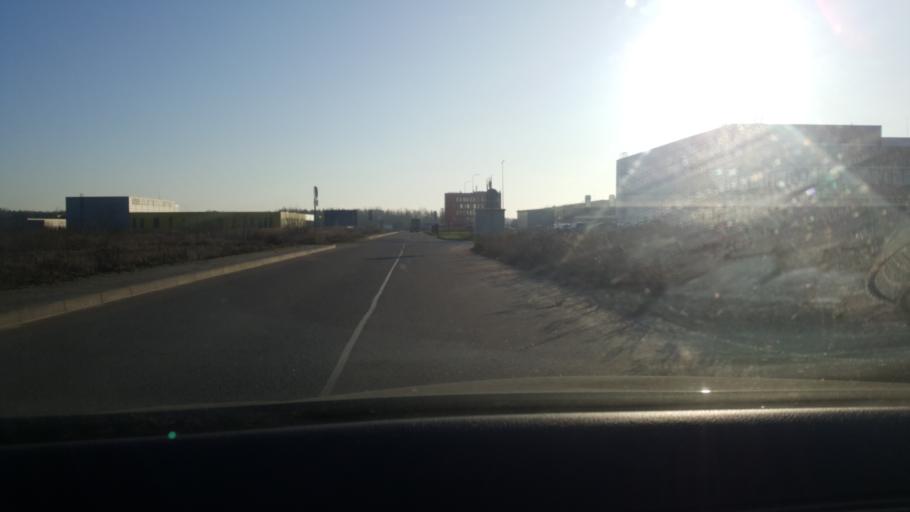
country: LT
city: Ramuciai
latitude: 54.9322
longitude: 24.0355
